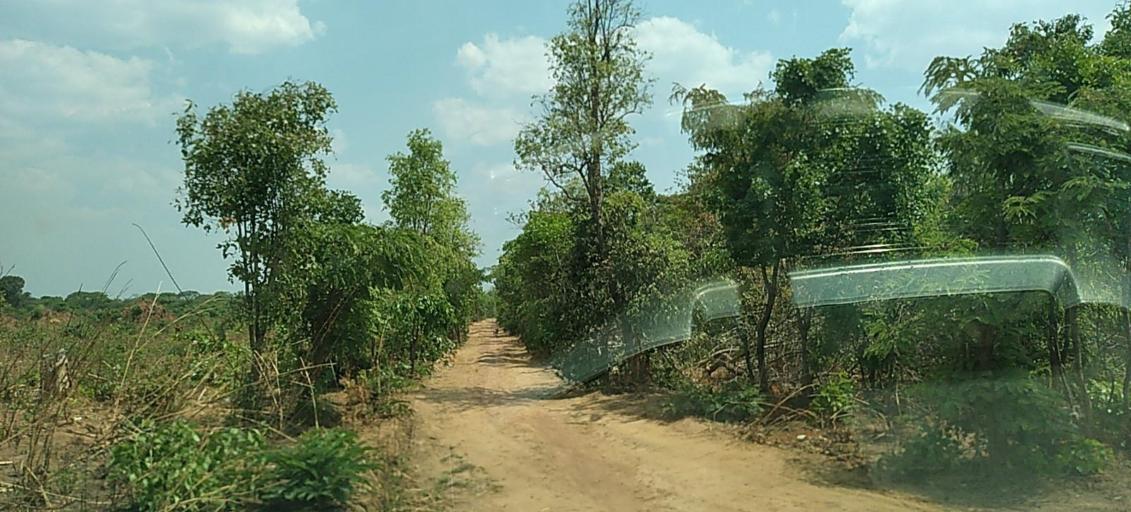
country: CD
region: Katanga
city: Kipushi
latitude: -12.0175
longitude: 27.4340
